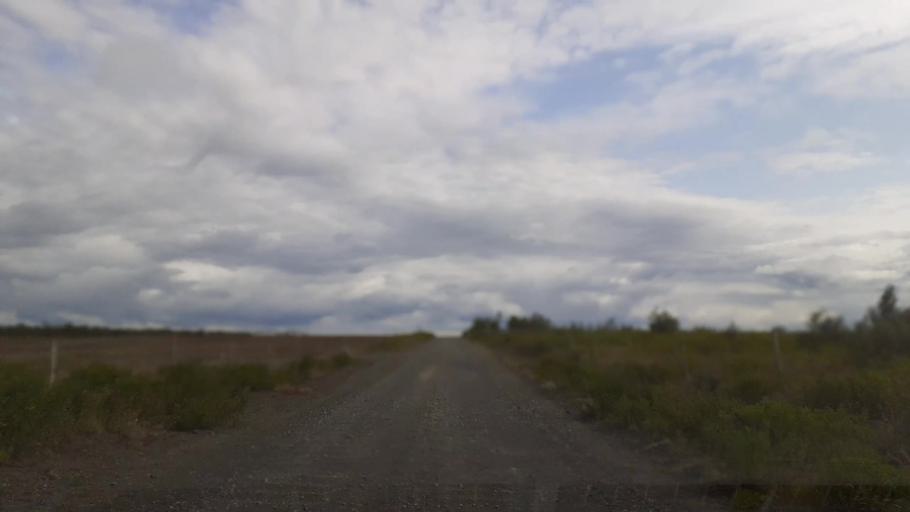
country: IS
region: South
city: Vestmannaeyjar
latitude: 63.8205
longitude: -20.3739
